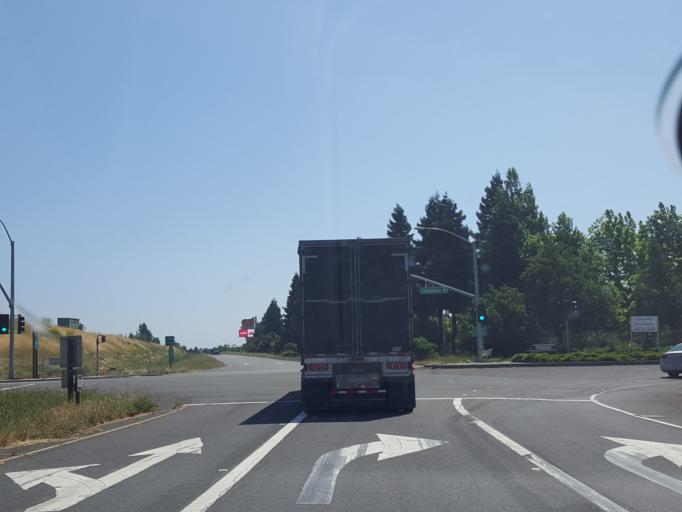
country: US
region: California
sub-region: Solano County
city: Suisun
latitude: 38.2393
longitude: -122.0847
